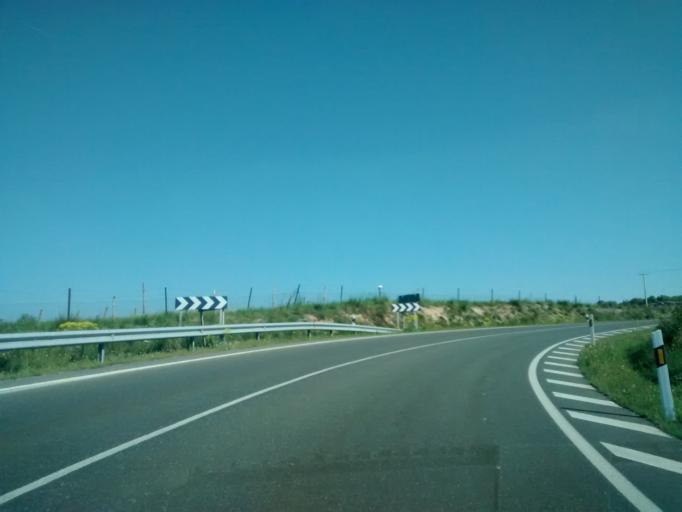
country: ES
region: Castille and Leon
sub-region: Provincia de Segovia
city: San Ildefonso
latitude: 40.9151
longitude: -4.0187
